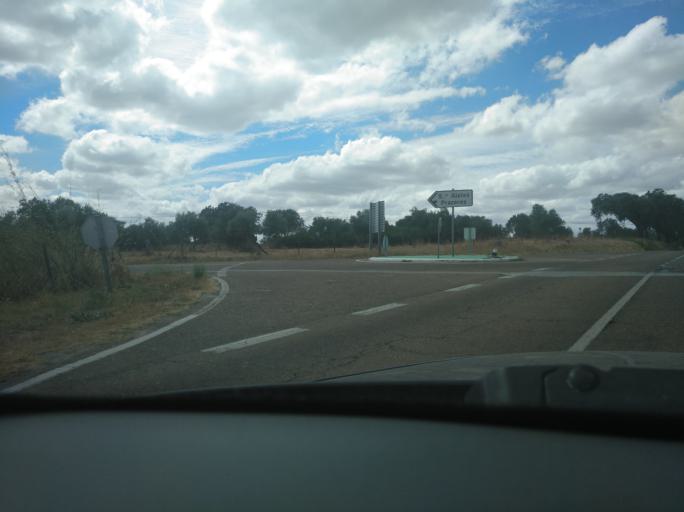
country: PT
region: Portalegre
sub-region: Arronches
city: Arronches
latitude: 39.0453
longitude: -7.4297
